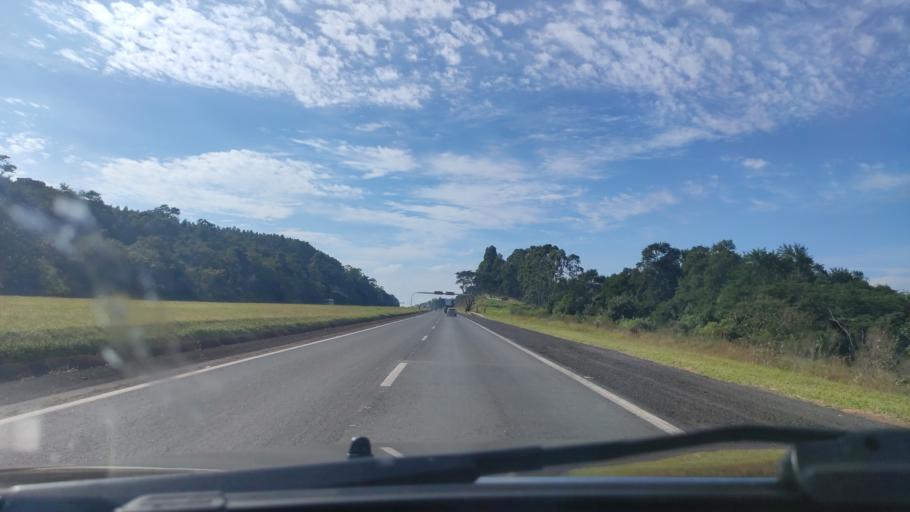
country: BR
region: Sao Paulo
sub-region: Itatinga
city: Itatinga
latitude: -23.0590
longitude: -48.5761
